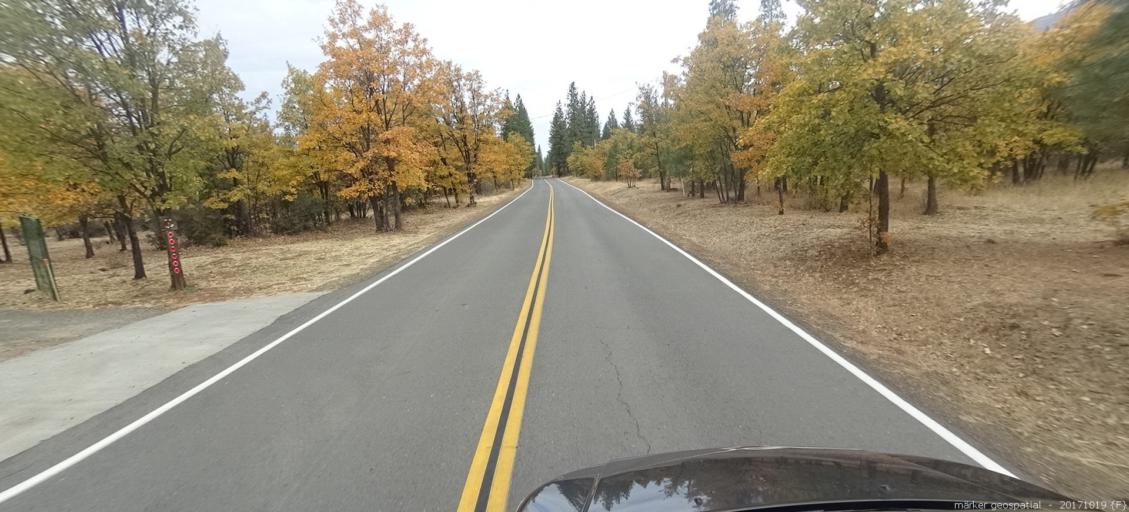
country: US
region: California
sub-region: Shasta County
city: Burney
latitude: 41.1667
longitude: -121.3587
